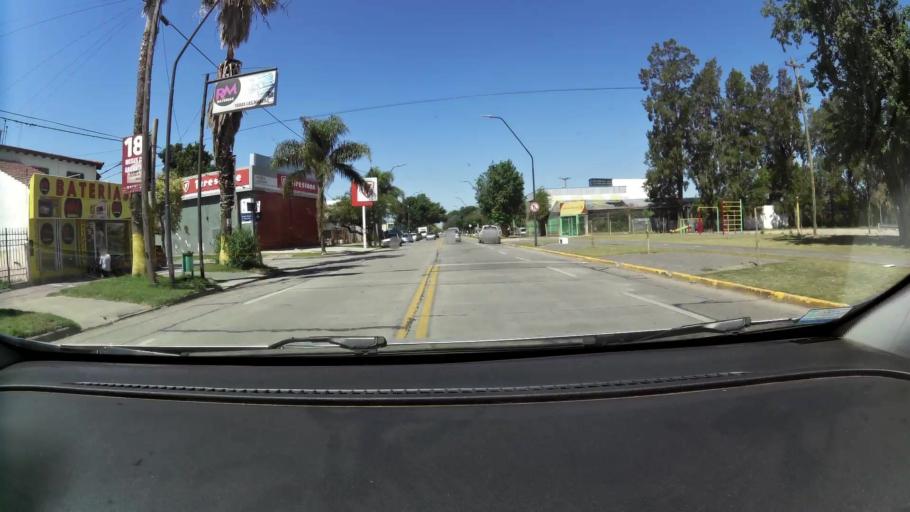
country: AR
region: Cordoba
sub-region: Departamento de Capital
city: Cordoba
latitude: -31.3793
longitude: -64.1432
